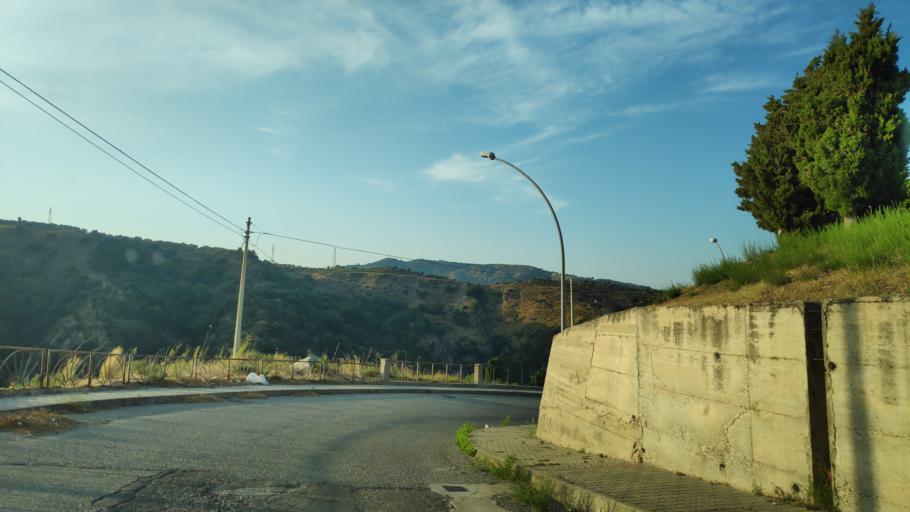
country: IT
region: Calabria
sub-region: Provincia di Catanzaro
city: Satriano
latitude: 38.6701
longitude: 16.4813
